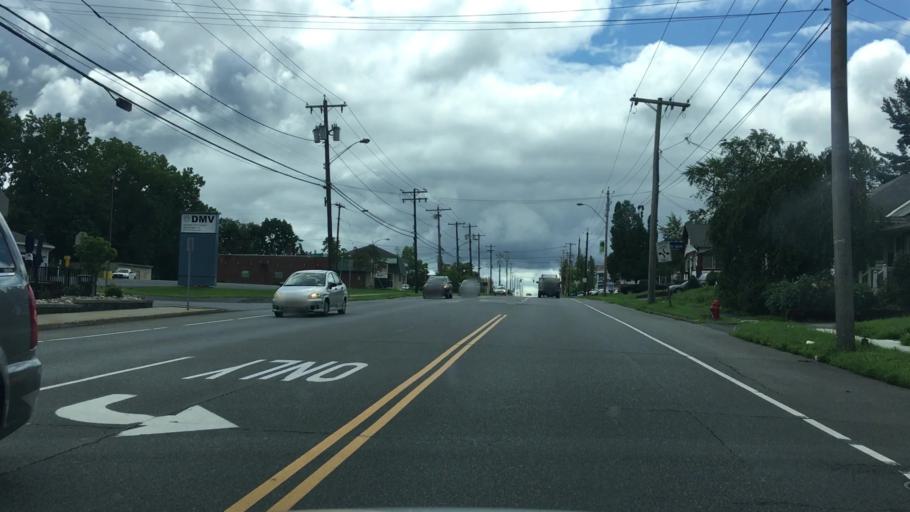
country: US
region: New York
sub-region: Schenectady County
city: Niskayuna
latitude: 42.7756
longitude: -73.8988
